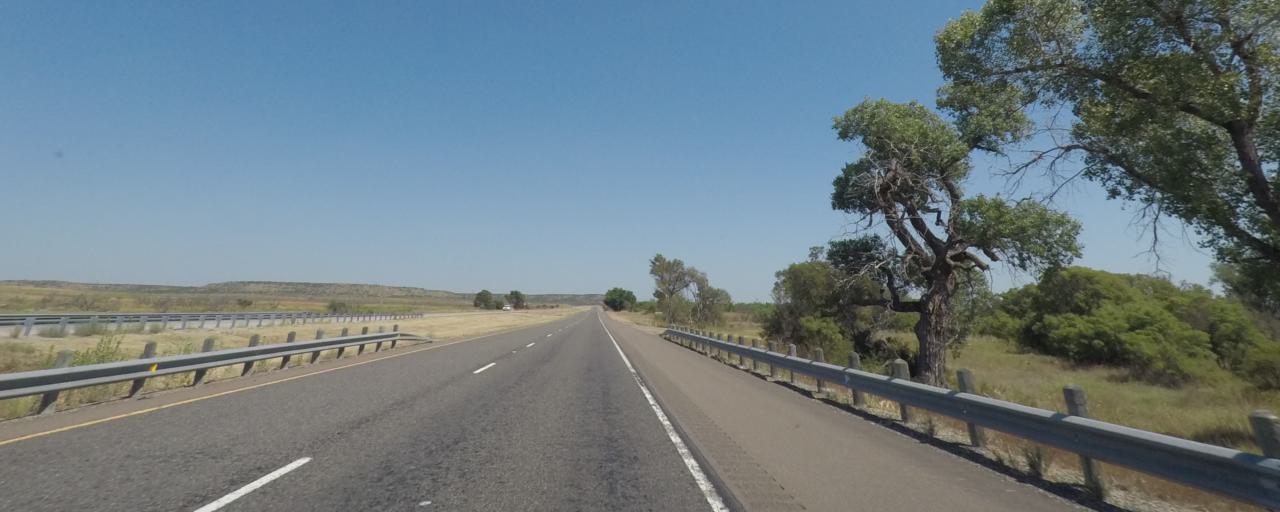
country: US
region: Texas
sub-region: Dickens County
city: Dickens
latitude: 33.6372
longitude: -100.9009
